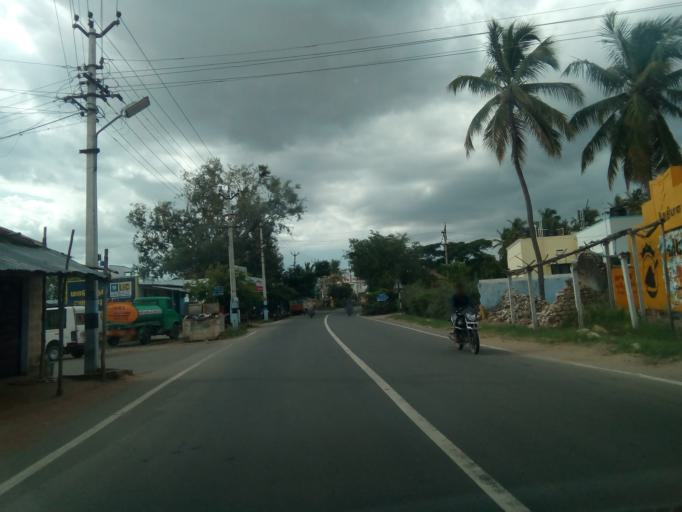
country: IN
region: Tamil Nadu
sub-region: Coimbatore
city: Irugur
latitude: 11.0806
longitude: 77.0355
